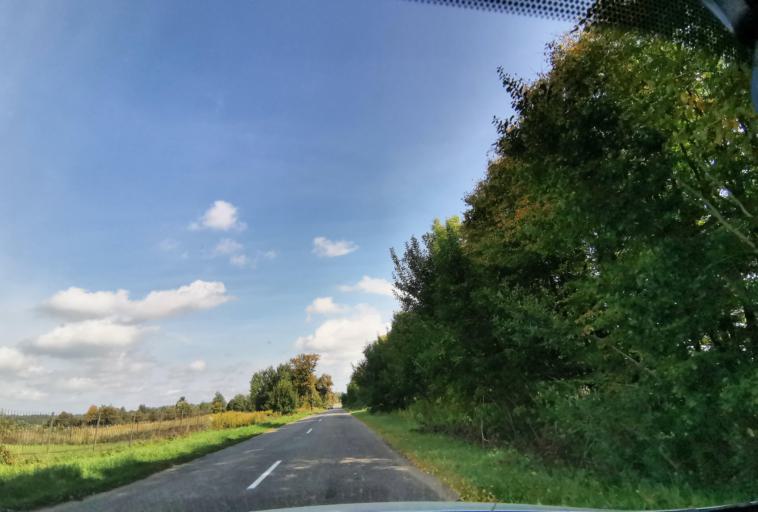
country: RU
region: Kaliningrad
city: Chernyakhovsk
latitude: 54.6551
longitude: 21.8936
